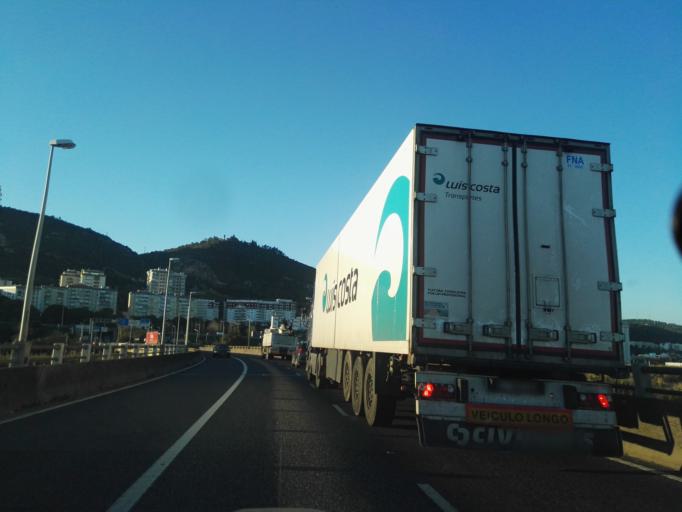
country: PT
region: Lisbon
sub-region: Vila Franca de Xira
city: Vila Franca de Xira
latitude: 38.9596
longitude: -8.9829
